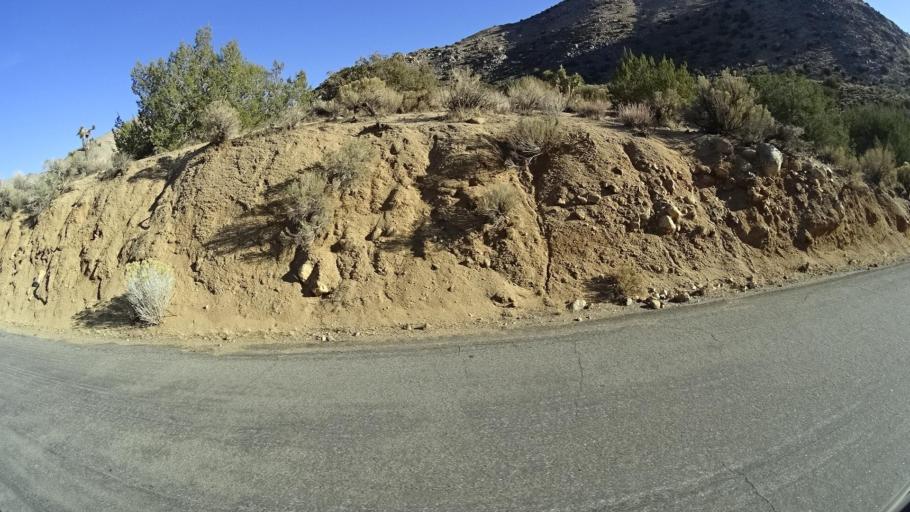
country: US
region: California
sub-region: Kern County
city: Weldon
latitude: 35.5834
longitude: -118.2478
